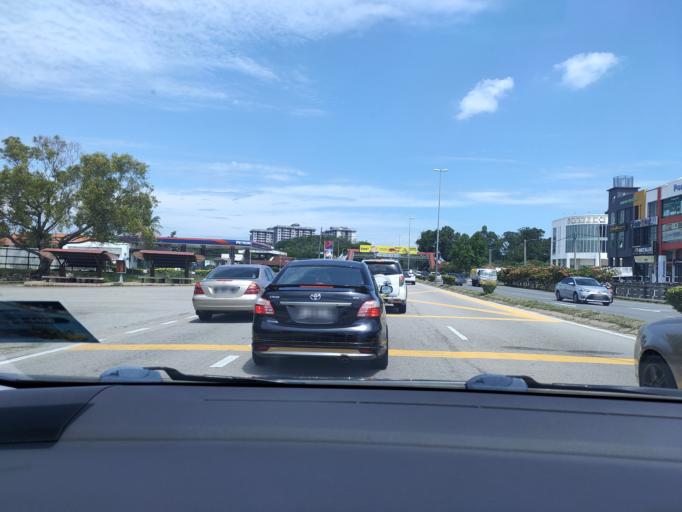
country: MY
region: Melaka
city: Batu Berendam
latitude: 2.2526
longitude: 102.2228
